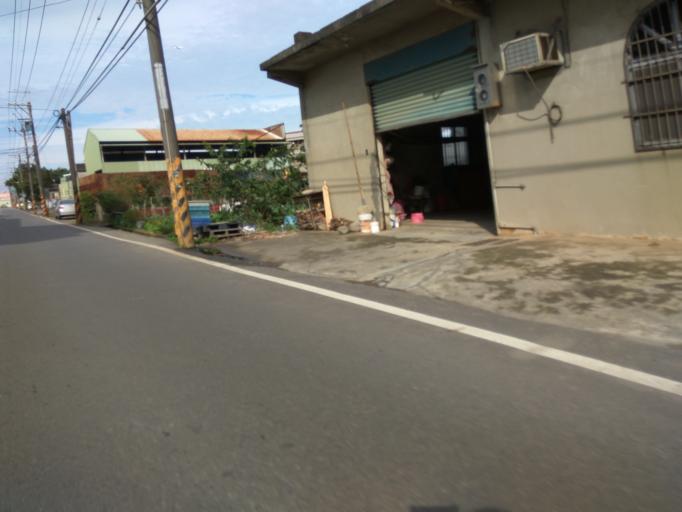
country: TW
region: Taiwan
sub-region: Hsinchu
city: Zhubei
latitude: 24.9515
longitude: 121.1325
